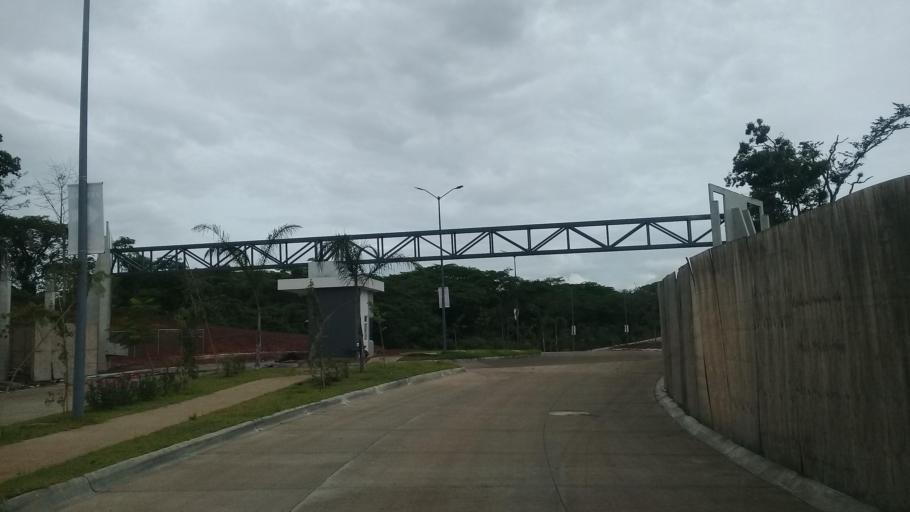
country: MX
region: Veracruz
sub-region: Emiliano Zapata
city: Jacarandas
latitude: 19.4879
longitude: -96.8505
